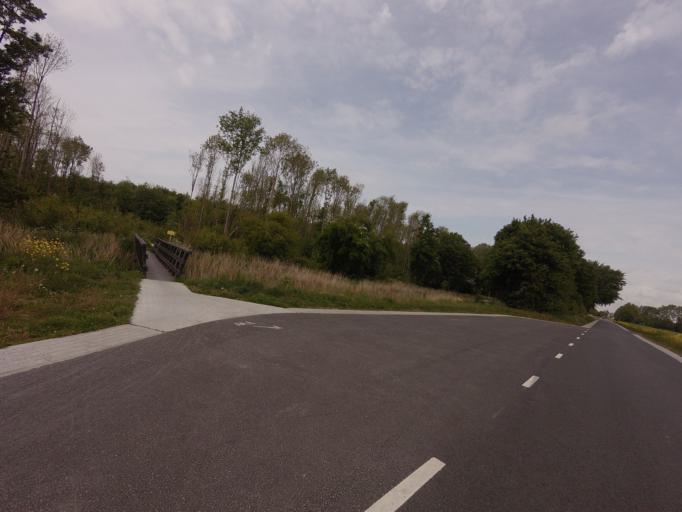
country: NL
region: Friesland
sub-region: Sudwest Fryslan
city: Bolsward
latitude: 53.0951
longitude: 5.4777
